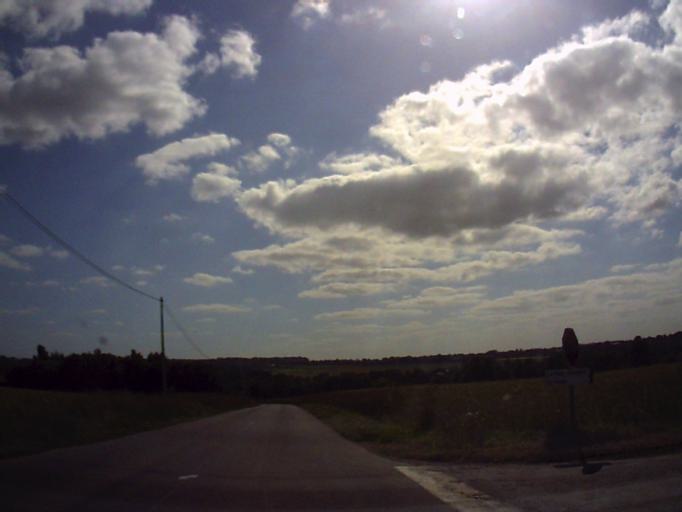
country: FR
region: Brittany
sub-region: Departement d'Ille-et-Vilaine
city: Bedee
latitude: 48.1730
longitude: -1.9890
